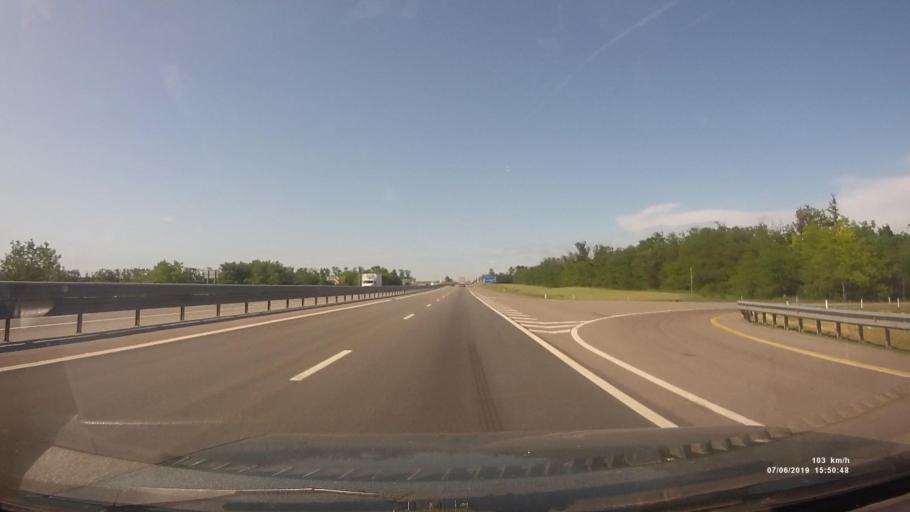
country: RU
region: Rostov
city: Gornyy
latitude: 47.8107
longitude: 40.1727
